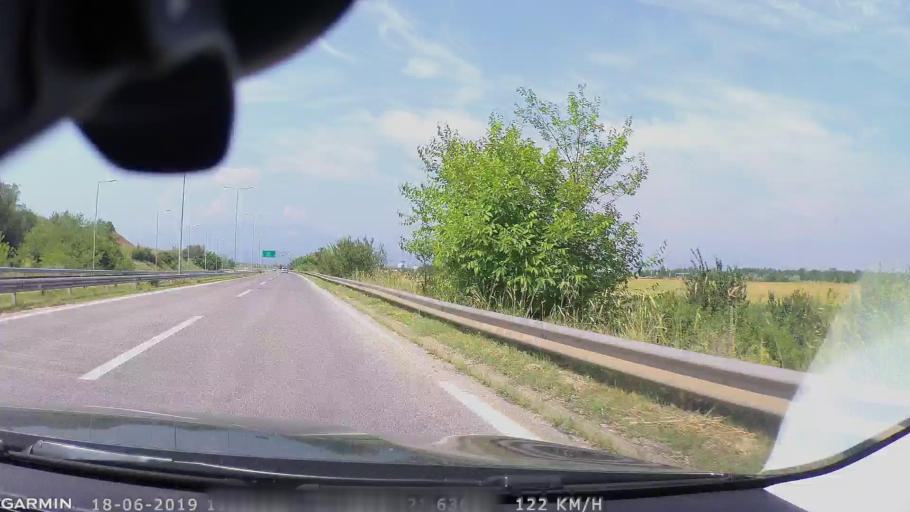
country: MK
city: Miladinovci
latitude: 41.9632
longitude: 21.6355
